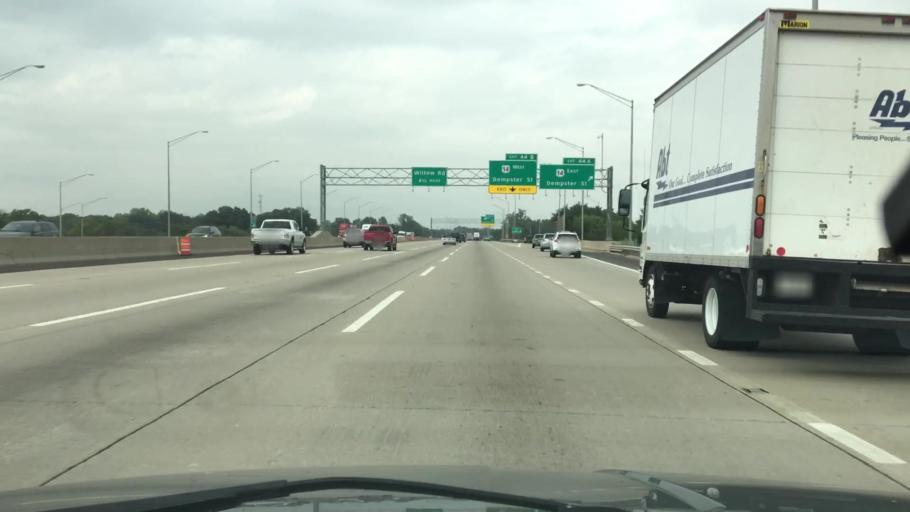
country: US
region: Illinois
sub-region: Cook County
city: Des Plaines
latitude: 42.0356
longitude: -87.8671
